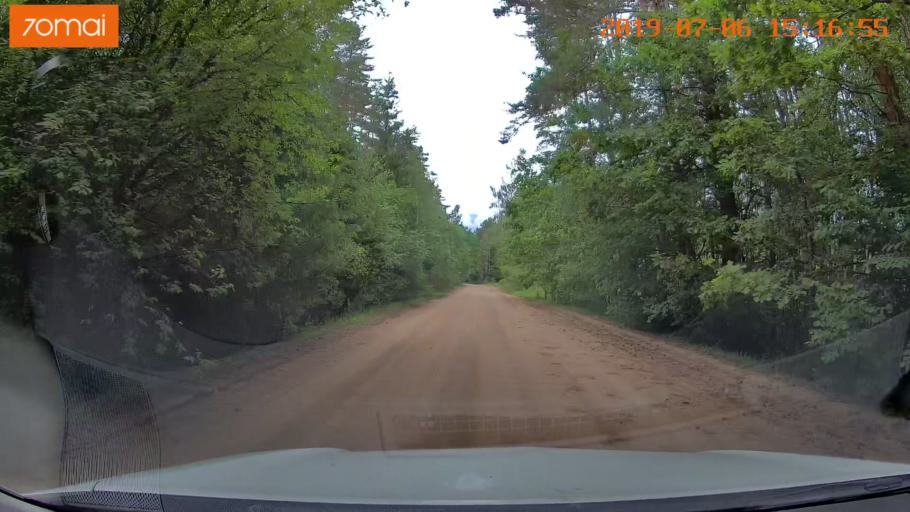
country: BY
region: Minsk
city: Ivyanyets
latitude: 53.9846
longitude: 26.6724
